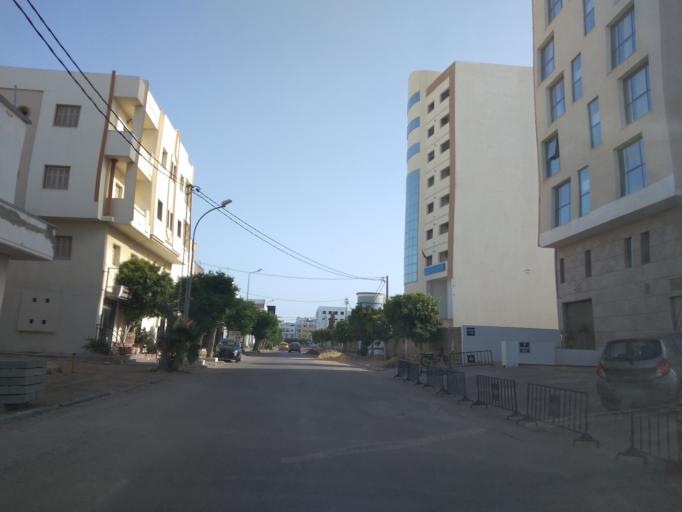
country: TN
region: Safaqis
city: Sfax
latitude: 34.7300
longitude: 10.7574
